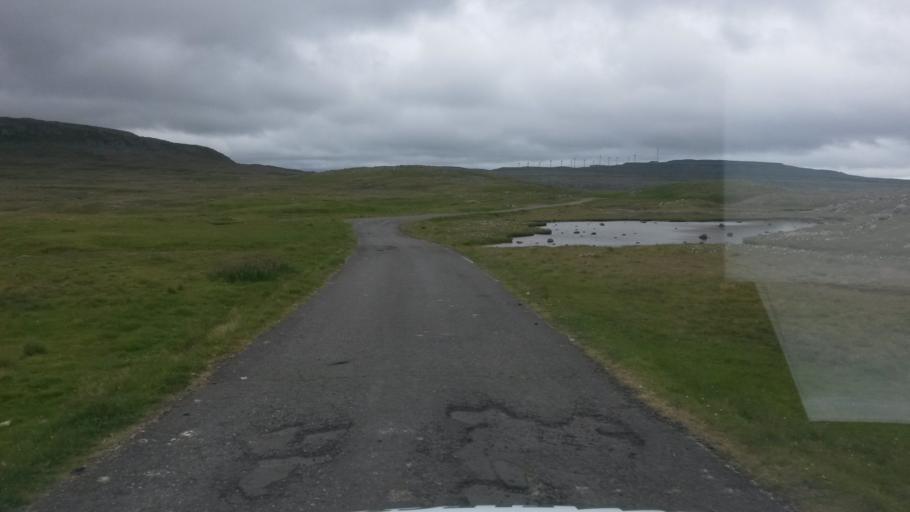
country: FO
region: Streymoy
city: Argir
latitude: 61.9921
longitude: -6.8490
